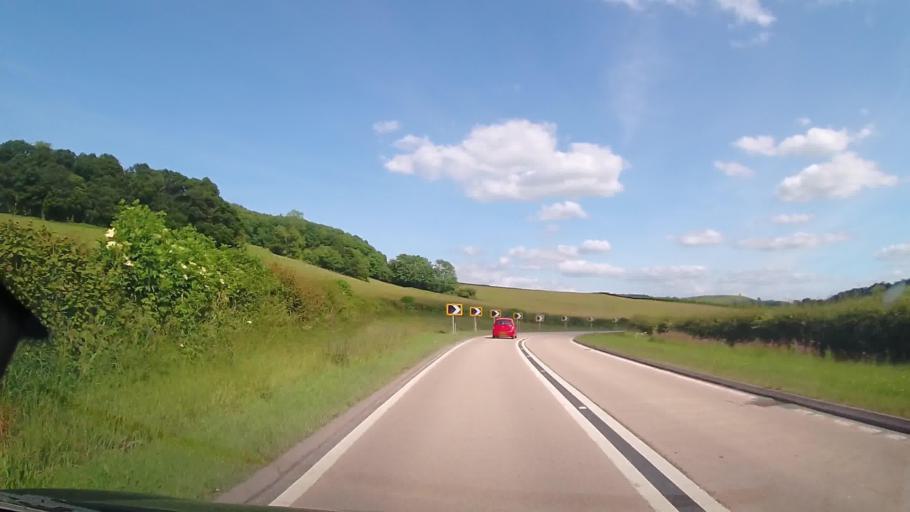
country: GB
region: Wales
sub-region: Sir Powys
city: Welshpool
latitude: 52.6535
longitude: -3.2535
